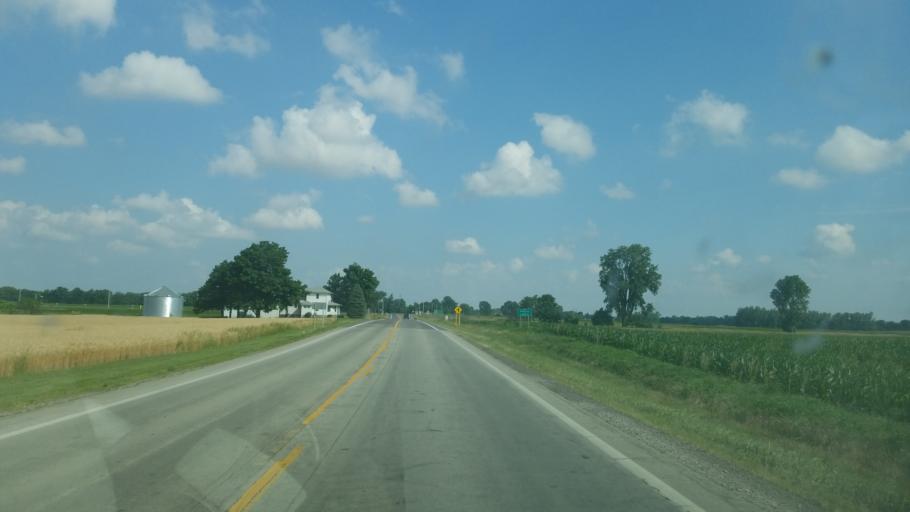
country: US
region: Ohio
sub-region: Logan County
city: Russells Point
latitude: 40.5285
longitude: -83.8301
